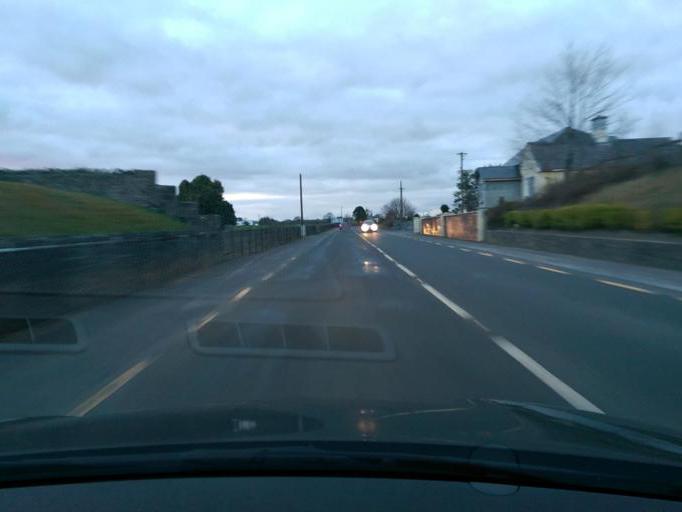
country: IE
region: Connaught
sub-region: County Galway
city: Portumna
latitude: 53.0998
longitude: -8.2291
